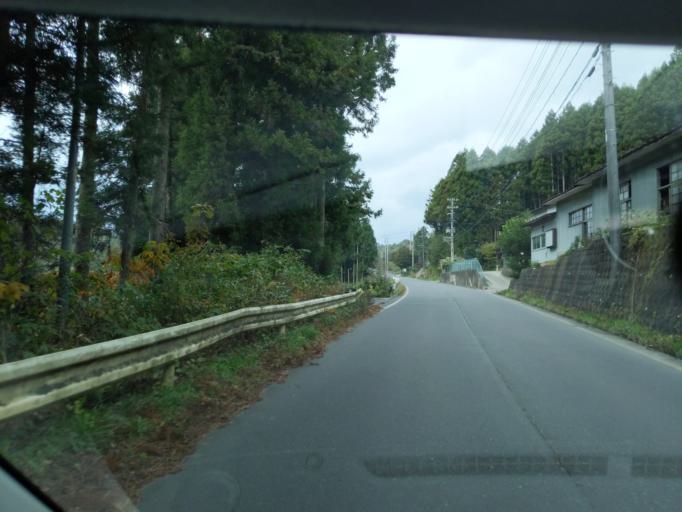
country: JP
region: Iwate
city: Mizusawa
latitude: 39.0470
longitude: 141.1148
